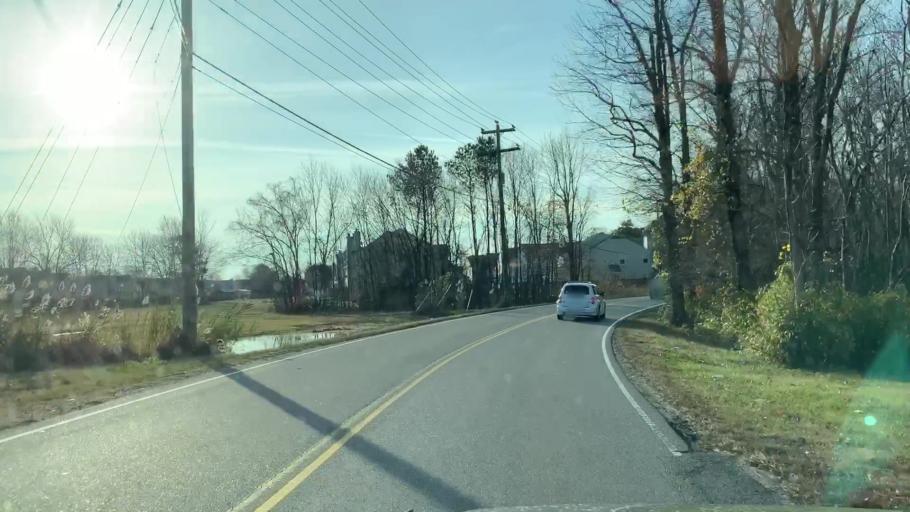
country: US
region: Virginia
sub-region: City of Chesapeake
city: Chesapeake
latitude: 36.7832
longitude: -76.1587
